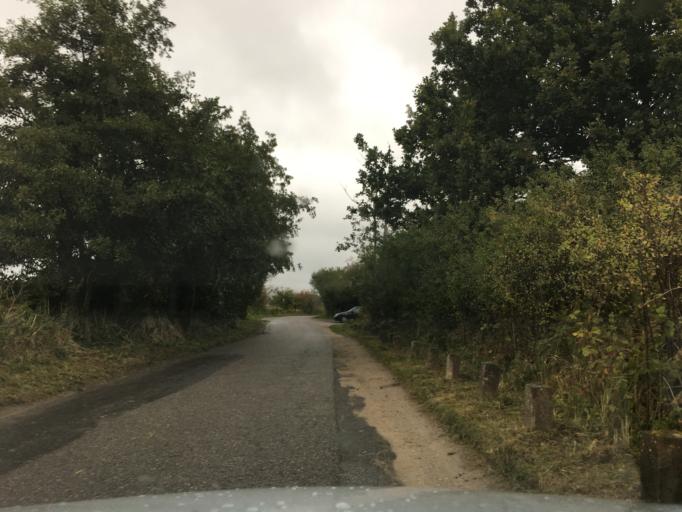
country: DE
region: Schleswig-Holstein
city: Strande
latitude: 54.4467
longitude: 10.1827
